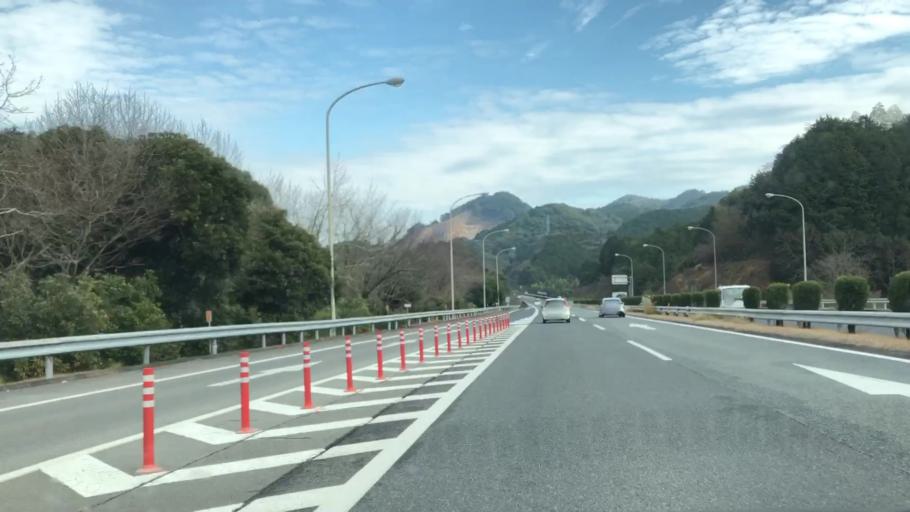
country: JP
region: Saga Prefecture
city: Takeocho-takeo
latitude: 33.1606
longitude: 130.0189
